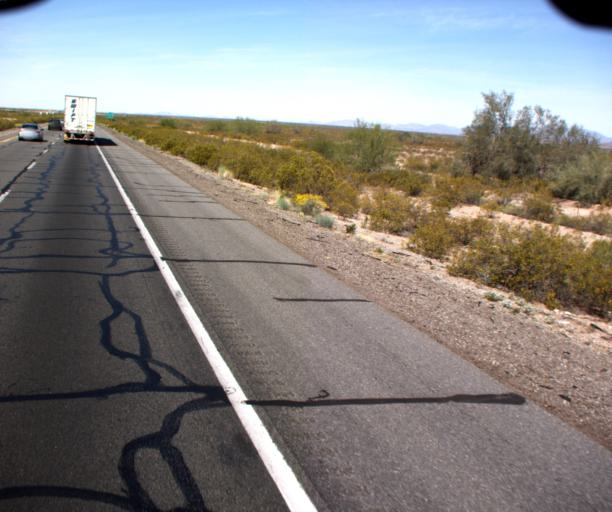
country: US
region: Arizona
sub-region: La Paz County
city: Salome
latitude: 33.5323
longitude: -113.1301
